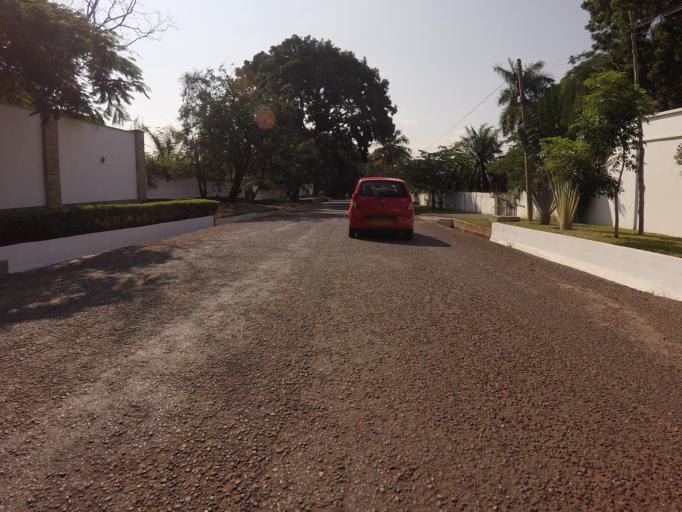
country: GH
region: Greater Accra
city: Accra
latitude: 5.5782
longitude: -0.1618
